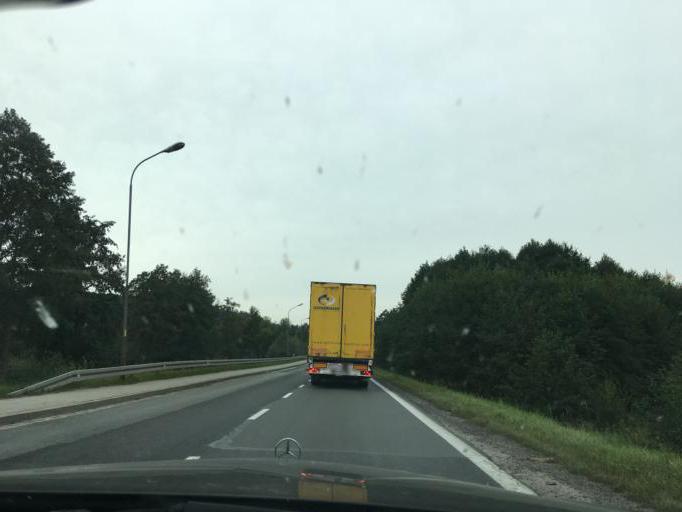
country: PL
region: Lower Silesian Voivodeship
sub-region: Powiat klodzki
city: Kudowa-Zdroj
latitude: 50.4349
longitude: 16.2242
